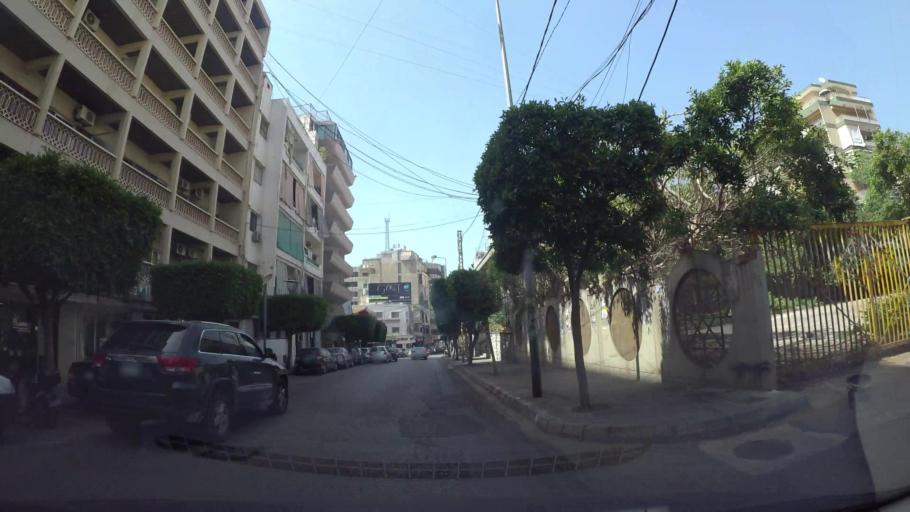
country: LB
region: Beyrouth
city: Ra's Bayrut
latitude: 33.8931
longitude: 35.4832
